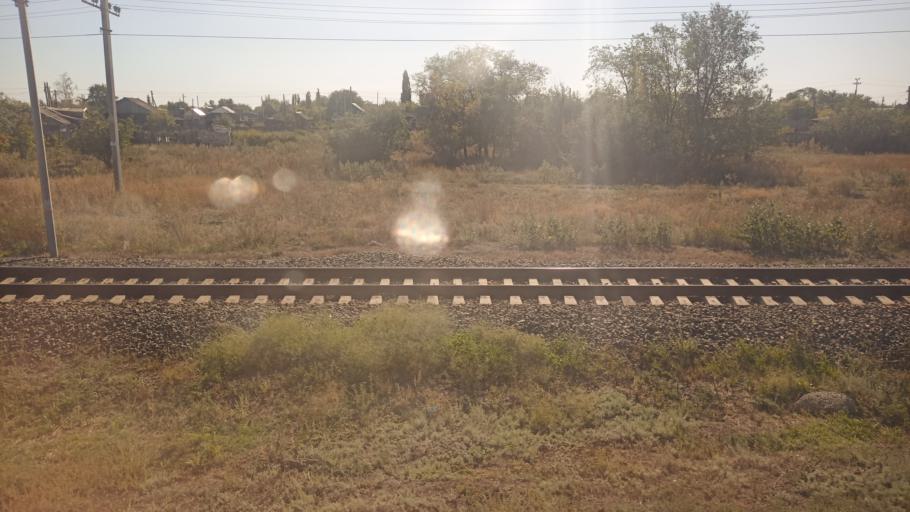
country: RU
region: Saratov
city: Pushkino
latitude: 51.2345
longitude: 46.9834
